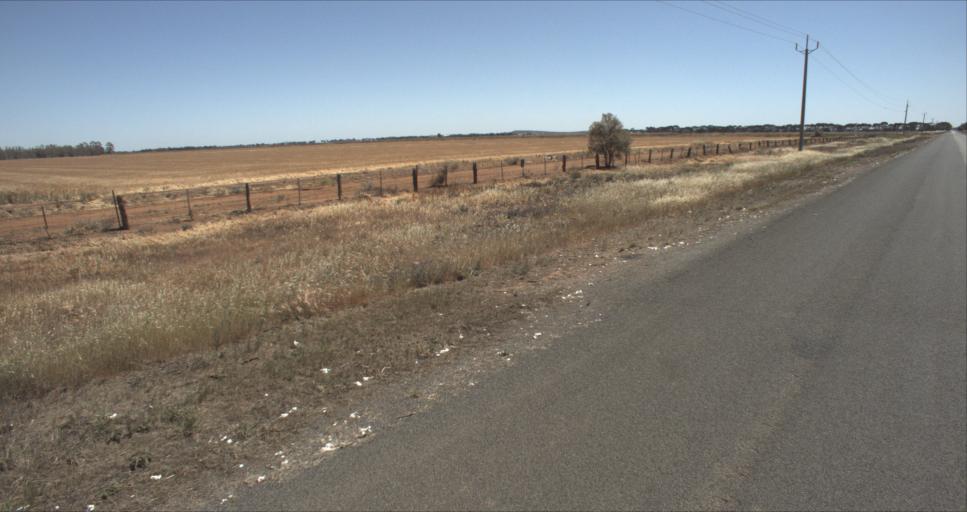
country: AU
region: New South Wales
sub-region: Leeton
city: Leeton
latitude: -34.4843
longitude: 146.2899
